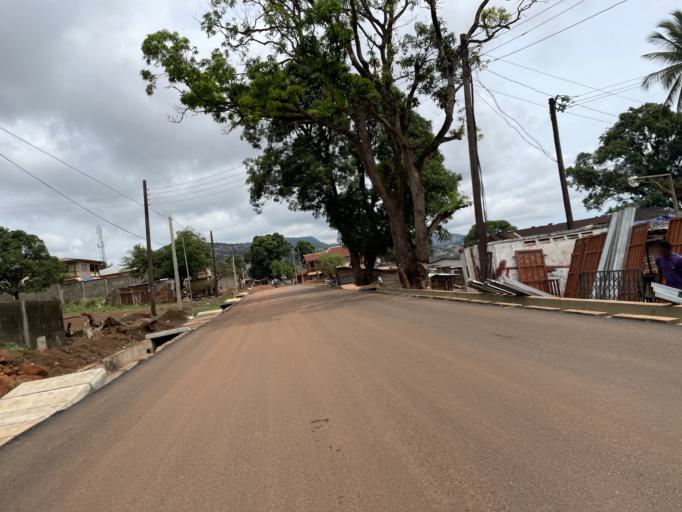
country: SL
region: Western Area
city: Hastings
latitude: 8.4122
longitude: -13.1460
